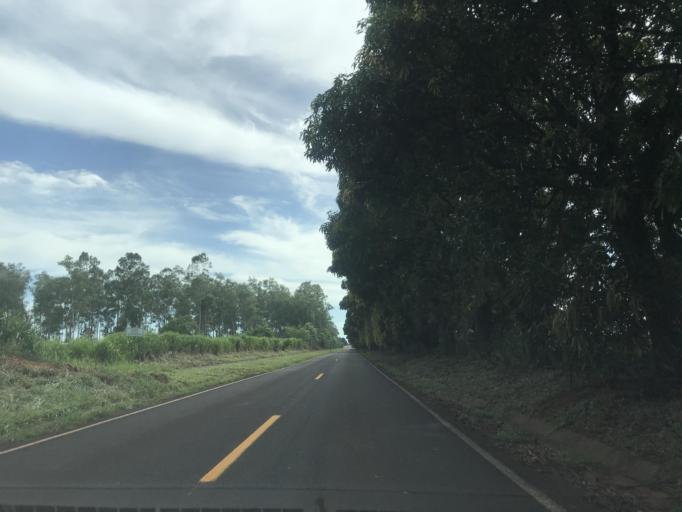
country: BR
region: Parana
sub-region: Terra Rica
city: Terra Rica
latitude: -22.7638
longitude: -52.6377
